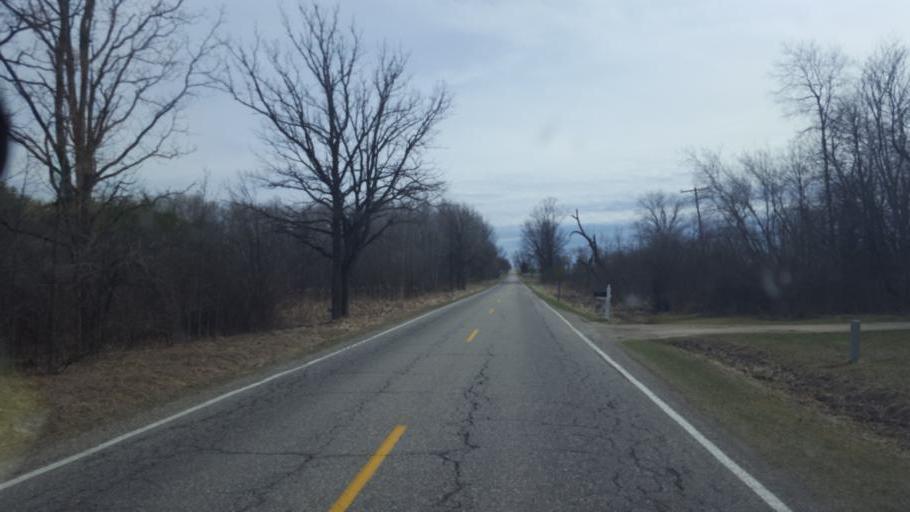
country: US
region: Michigan
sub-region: Montcalm County
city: Edmore
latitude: 43.5058
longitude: -85.0256
